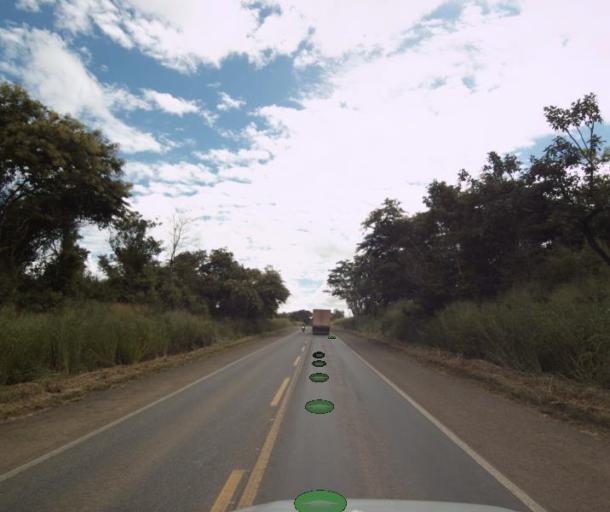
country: BR
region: Goias
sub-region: Uruacu
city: Uruacu
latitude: -14.4117
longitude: -49.1573
